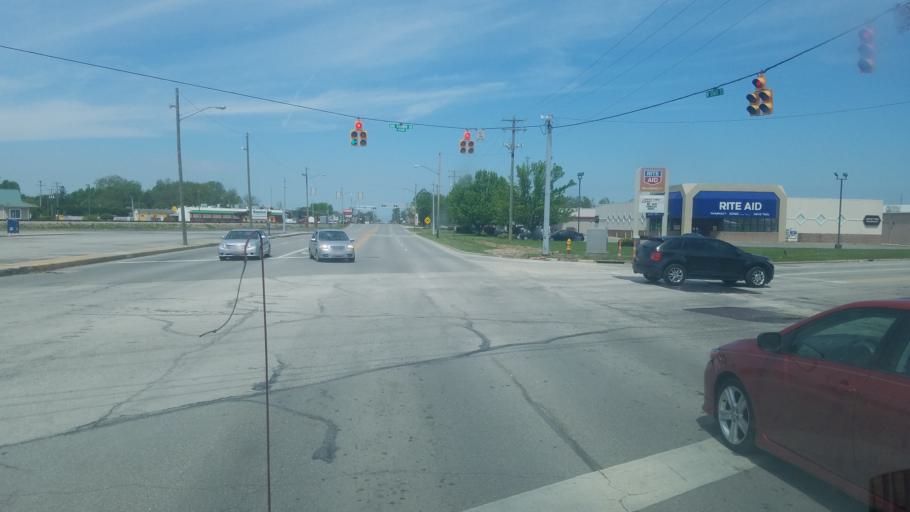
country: US
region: Ohio
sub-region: Sandusky County
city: Fremont
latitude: 41.3568
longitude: -83.1365
